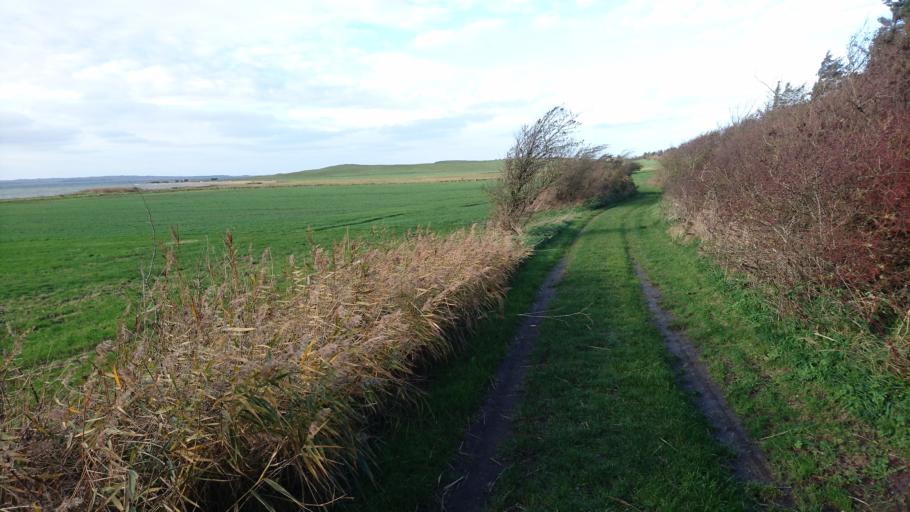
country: DK
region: North Denmark
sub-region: Vesthimmerland Kommune
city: Farso
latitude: 56.8028
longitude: 9.1806
